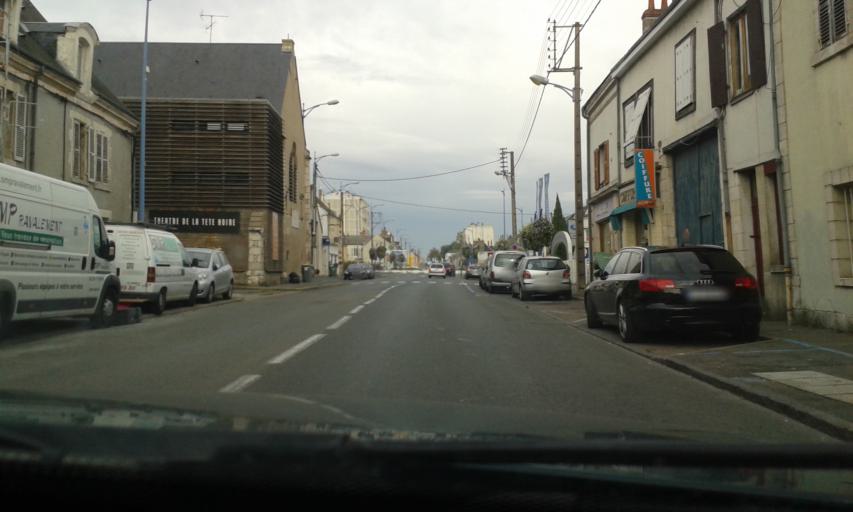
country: FR
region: Centre
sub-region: Departement du Loiret
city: Fleury-les-Aubrais
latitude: 47.9332
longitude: 1.8949
